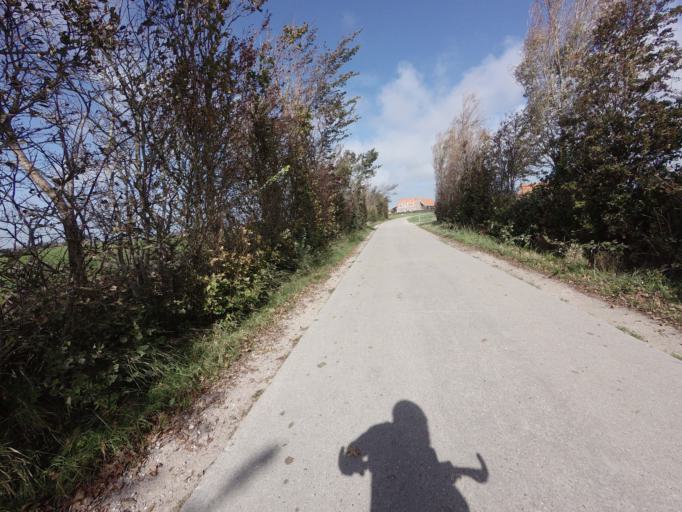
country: NL
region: Zeeland
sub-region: Gemeente Middelburg
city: Middelburg
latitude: 51.5340
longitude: 3.5251
